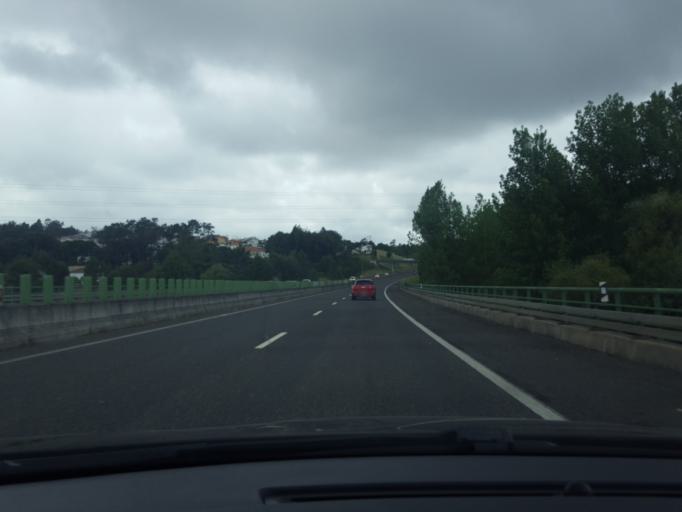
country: PT
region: Leiria
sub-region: Leiria
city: Leiria
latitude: 39.7504
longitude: -8.7751
